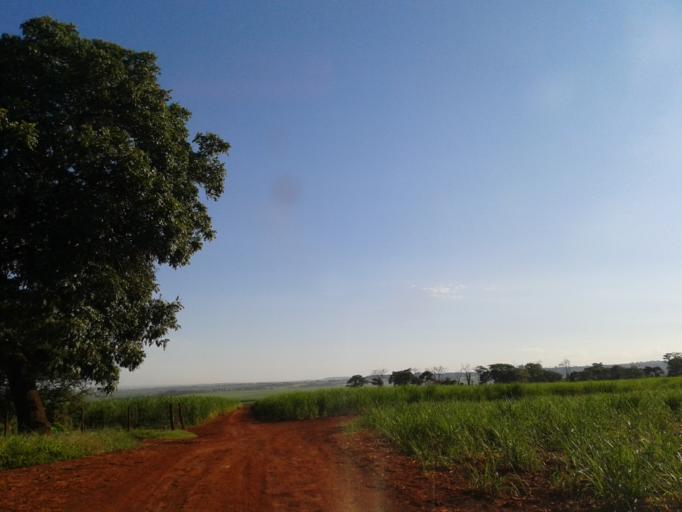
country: BR
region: Minas Gerais
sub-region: Centralina
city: Centralina
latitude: -18.6623
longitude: -49.2561
